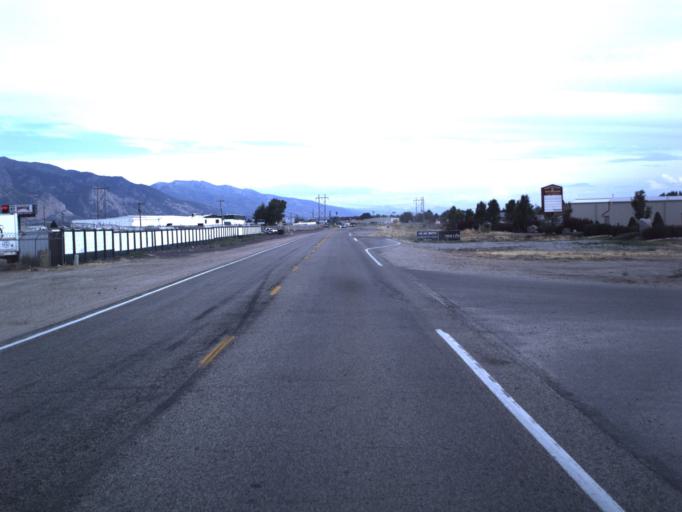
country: US
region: Utah
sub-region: Weber County
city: Farr West
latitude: 41.3242
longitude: -112.0314
